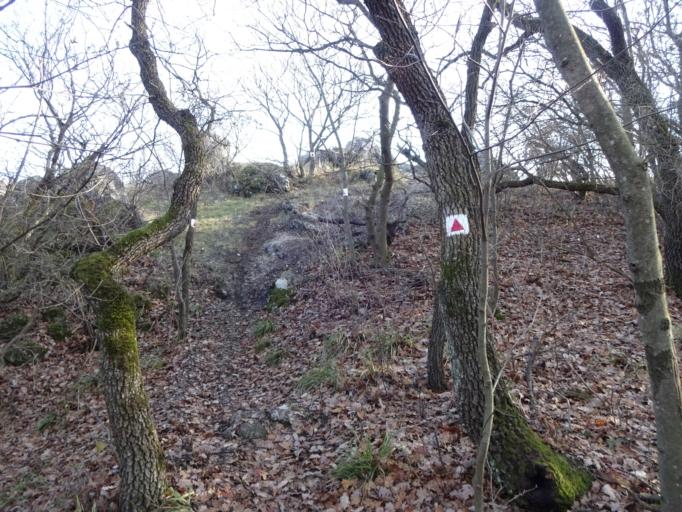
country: HU
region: Veszprem
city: Varpalota
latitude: 47.2208
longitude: 18.1941
